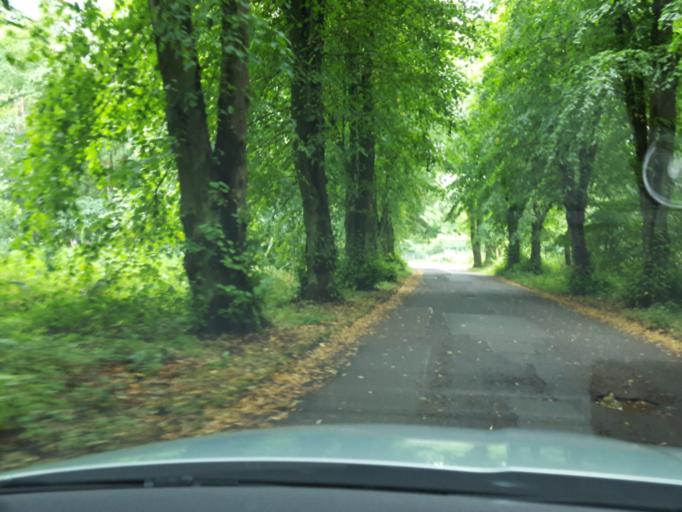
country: GB
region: Scotland
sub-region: Falkirk
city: Polmont
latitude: 55.9642
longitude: -3.6679
